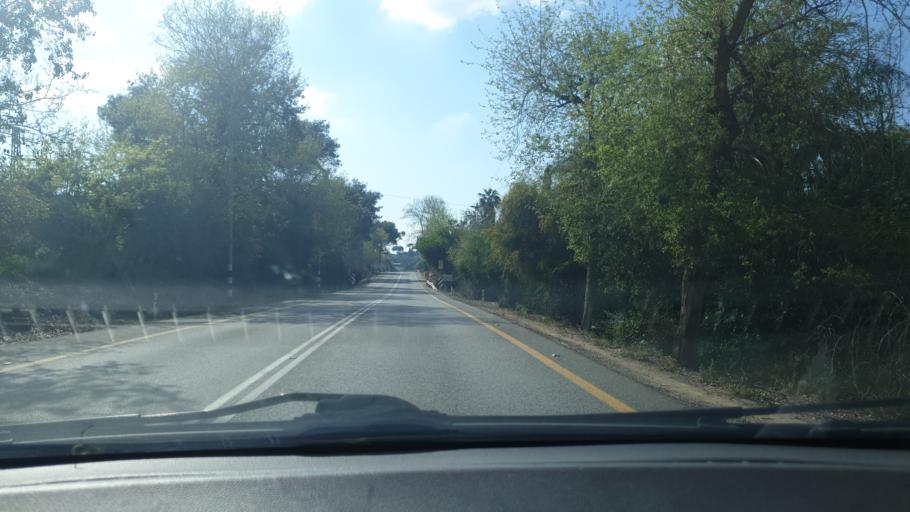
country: IL
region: Central District
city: Bet Yizhaq
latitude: 32.3441
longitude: 34.9138
